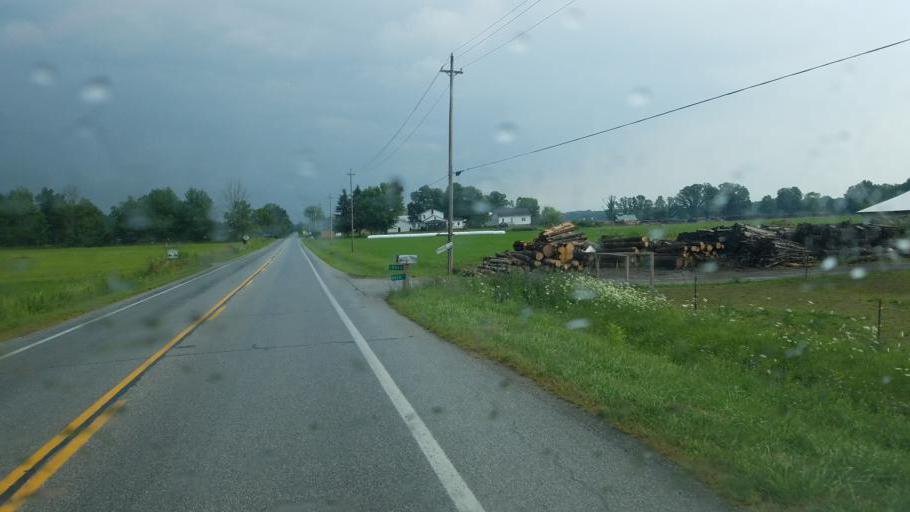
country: US
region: Ohio
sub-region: Ashtabula County
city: Orwell
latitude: 41.4894
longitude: -80.9464
